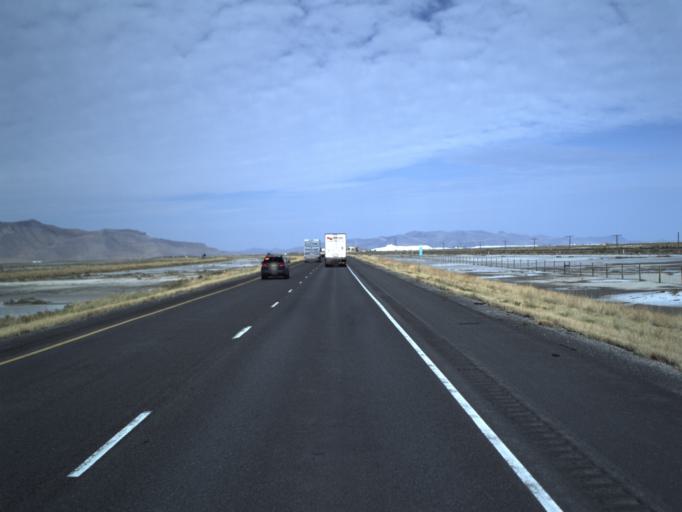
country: US
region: Utah
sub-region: Tooele County
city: Grantsville
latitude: 40.6983
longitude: -112.4808
